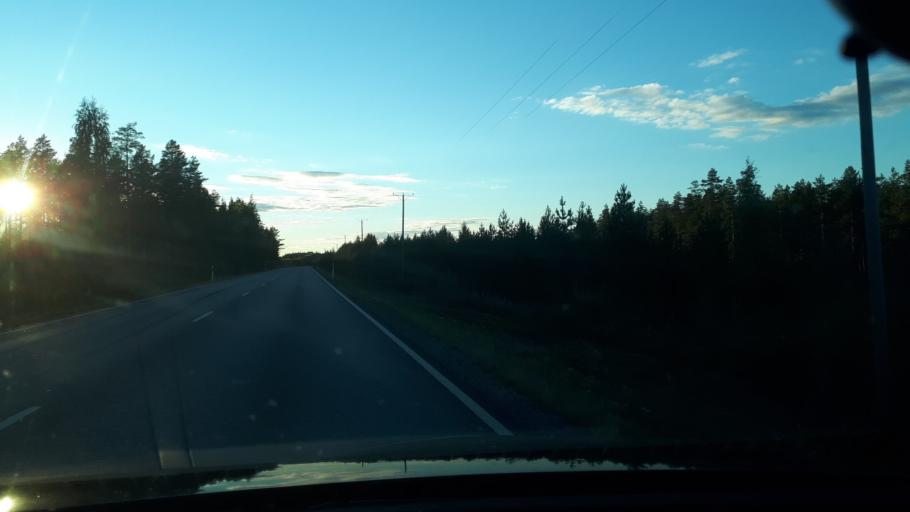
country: FI
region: Northern Ostrobothnia
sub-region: Haapavesi-Siikalatva
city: Pyhaentae
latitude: 64.1362
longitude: 26.2487
